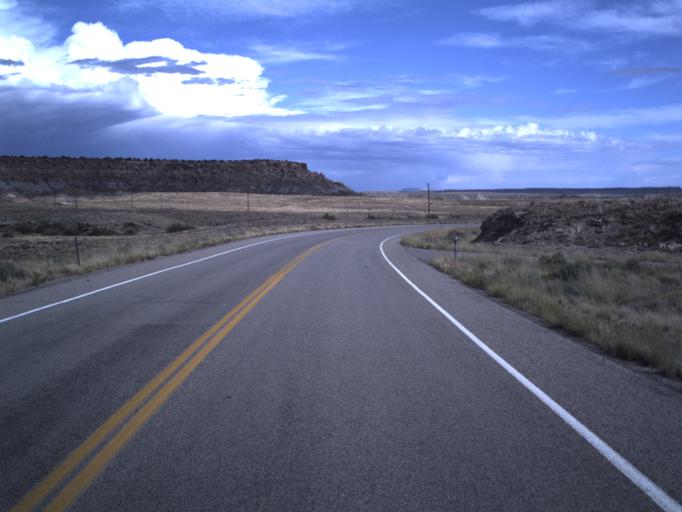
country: US
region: Colorado
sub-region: Montezuma County
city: Towaoc
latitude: 37.1655
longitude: -109.0757
